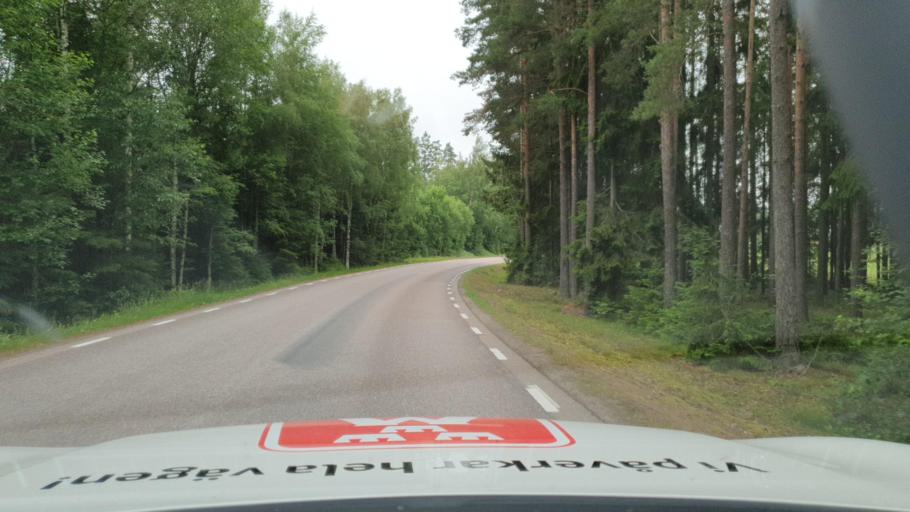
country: SE
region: Vaermland
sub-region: Kristinehamns Kommun
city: Kristinehamn
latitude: 59.4605
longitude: 13.9382
